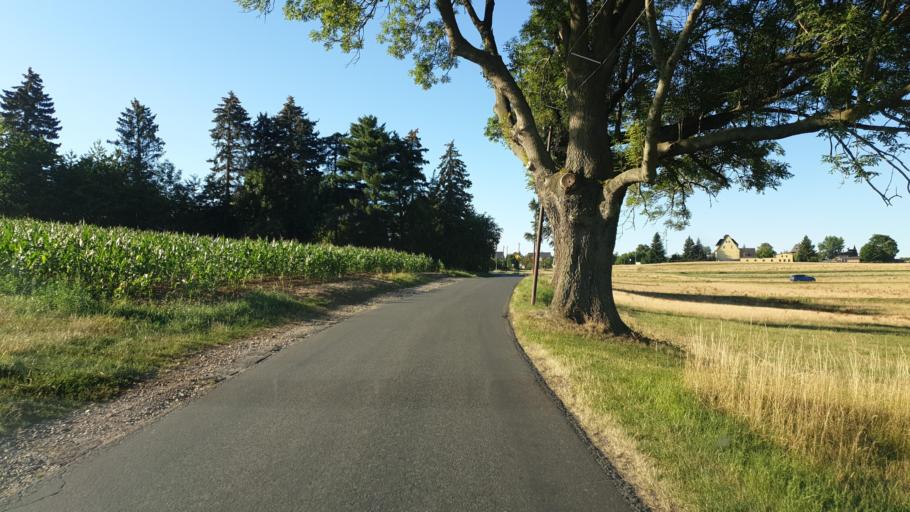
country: DE
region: Saxony
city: Lichtentanne
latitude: 50.6804
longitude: 12.4409
